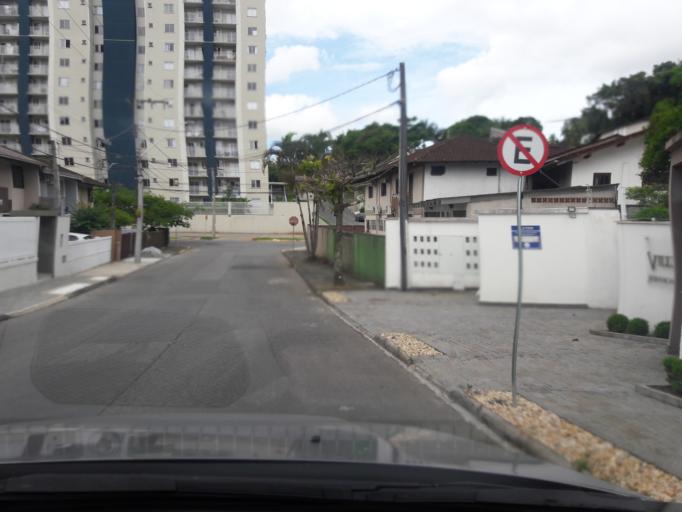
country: BR
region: Santa Catarina
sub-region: Joinville
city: Joinville
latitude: -26.3194
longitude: -48.8625
